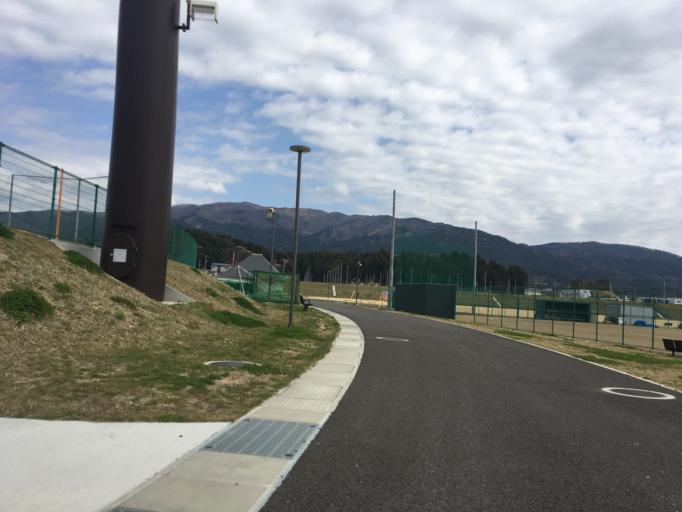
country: JP
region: Iwate
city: Ofunato
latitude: 39.0107
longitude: 141.6344
